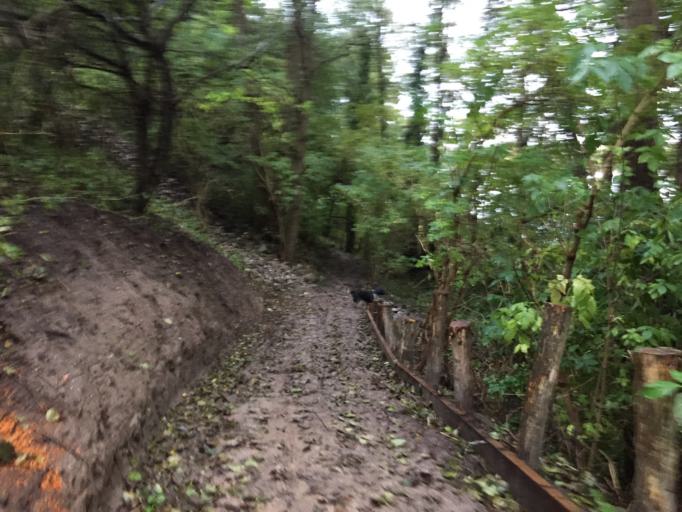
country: DK
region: Zealand
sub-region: Ringsted Kommune
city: Ringsted
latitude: 55.4887
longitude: 11.7767
